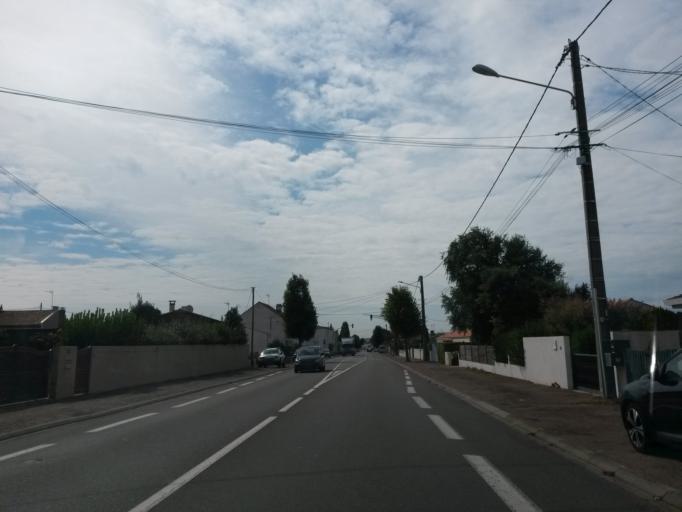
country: FR
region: Pays de la Loire
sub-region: Departement de la Vendee
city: Olonne-sur-Mer
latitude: 46.5202
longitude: -1.7756
